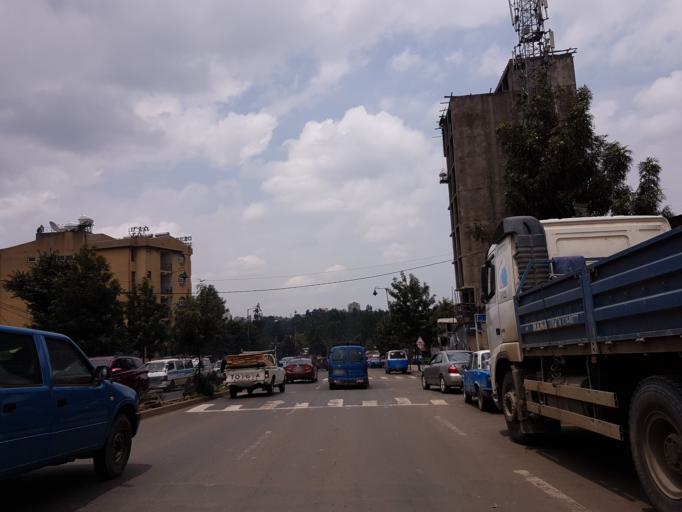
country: ET
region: Adis Abeba
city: Addis Ababa
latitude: 9.0082
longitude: 38.7339
